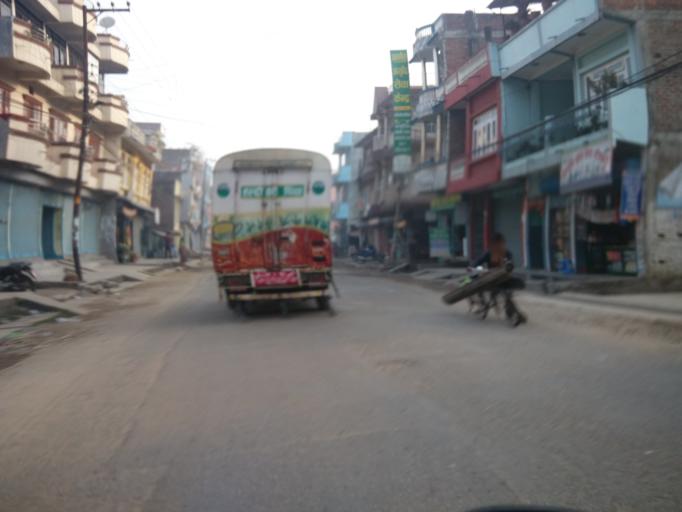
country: NP
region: Central Region
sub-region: Narayani Zone
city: Bharatpur
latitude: 27.6904
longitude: 84.4199
